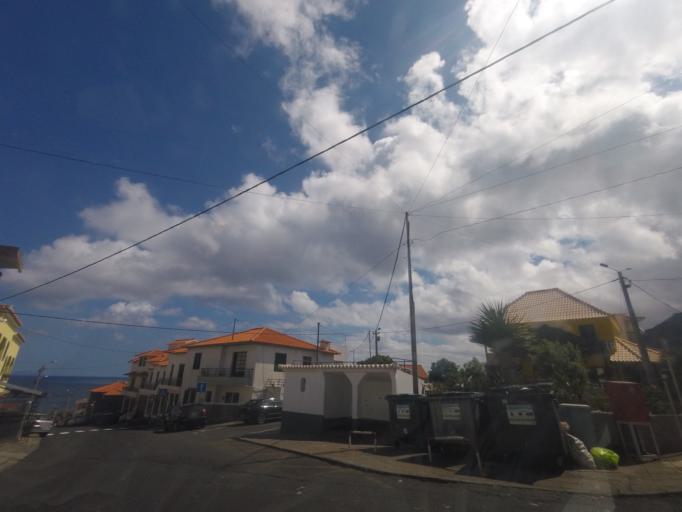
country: PT
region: Madeira
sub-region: Machico
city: Canical
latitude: 32.7398
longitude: -16.7409
